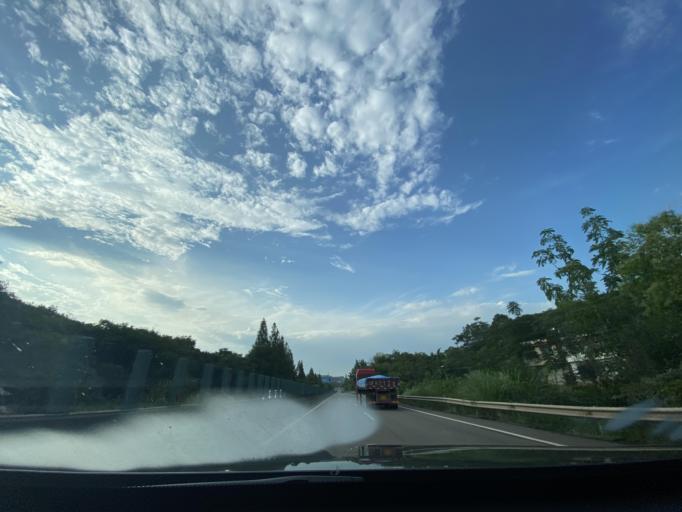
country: CN
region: Sichuan
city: Jiancheng
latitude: 30.3331
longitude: 104.5659
